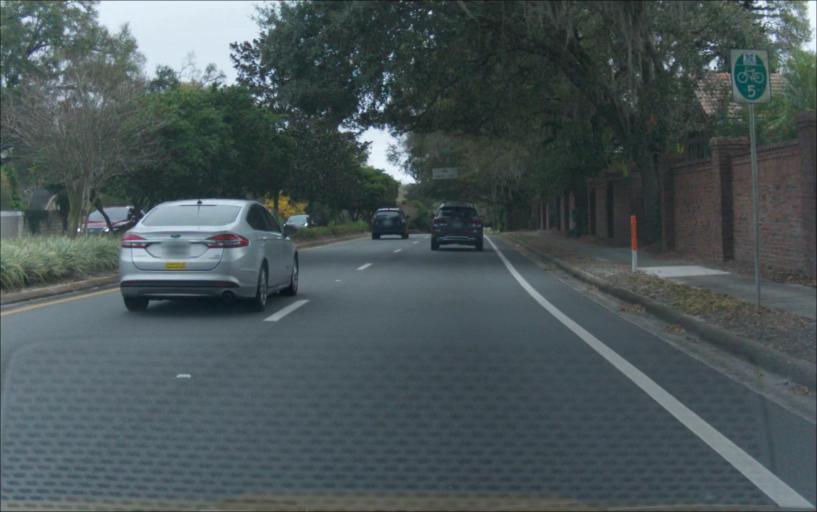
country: US
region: Florida
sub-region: Orange County
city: Winter Park
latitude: 28.6244
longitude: -81.3273
